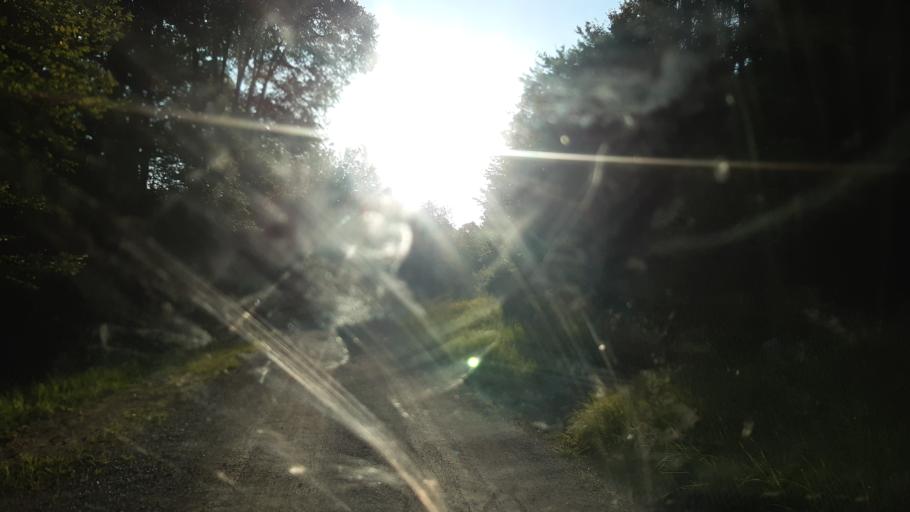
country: SI
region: Kocevje
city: Kocevje
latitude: 45.6660
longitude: 14.9515
